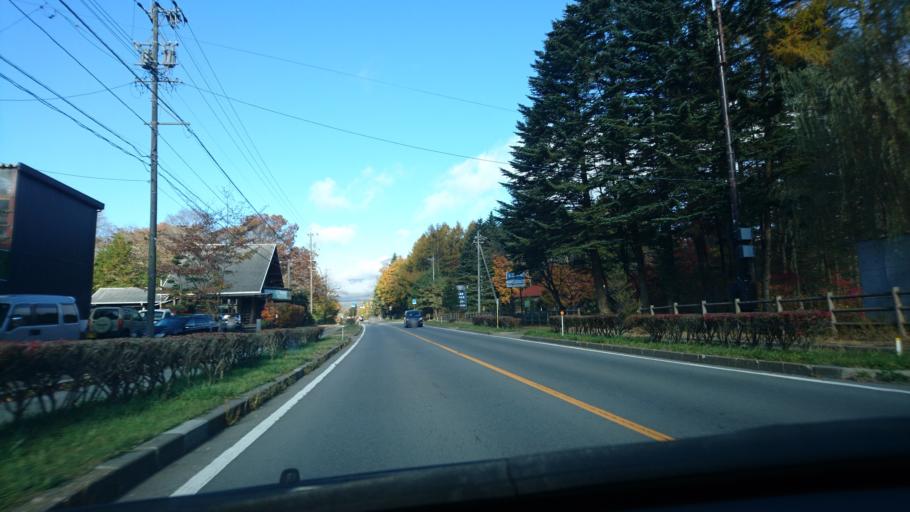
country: JP
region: Nagano
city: Saku
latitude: 36.3298
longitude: 138.6110
